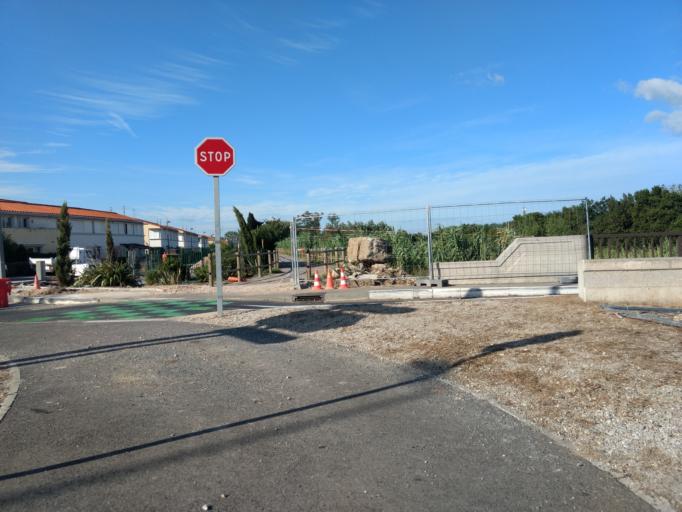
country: FR
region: Languedoc-Roussillon
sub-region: Departement des Pyrenees-Orientales
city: Saint-Laurent-de-la-Salanque
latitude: 42.7767
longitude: 2.9836
